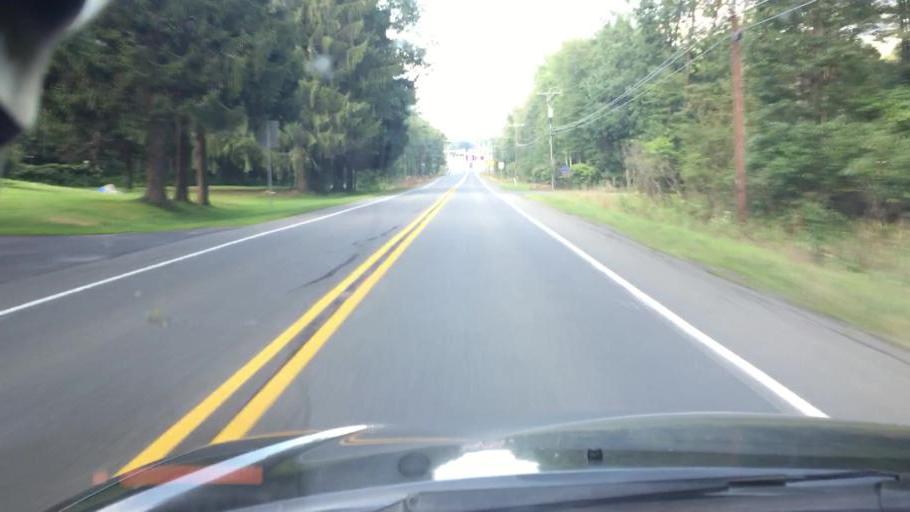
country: US
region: Pennsylvania
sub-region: Carbon County
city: Towamensing Trails
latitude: 40.9776
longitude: -75.6356
